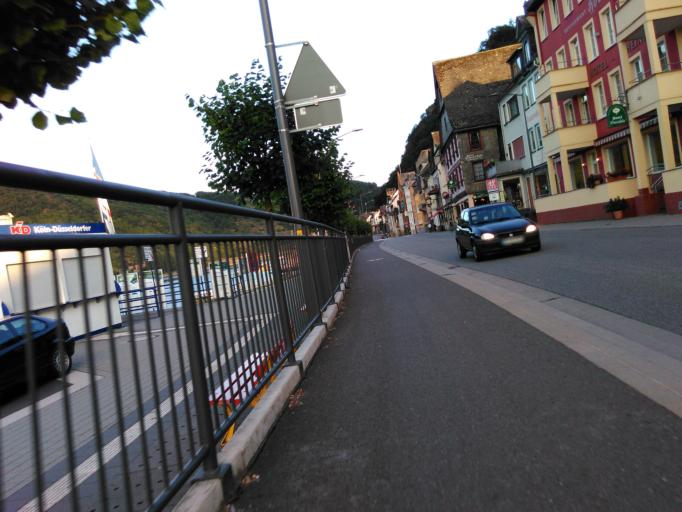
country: DE
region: Rheinland-Pfalz
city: Sankt Goar
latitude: 50.1509
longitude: 7.7157
